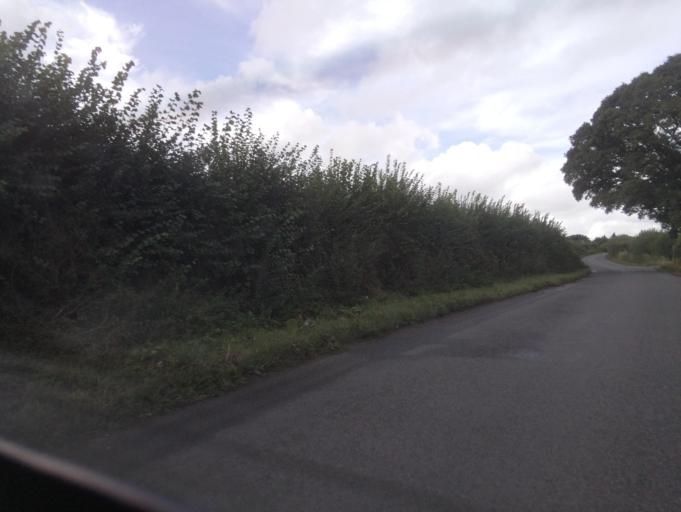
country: GB
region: England
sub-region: Worcestershire
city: Kidderminster
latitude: 52.3574
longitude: -2.1909
